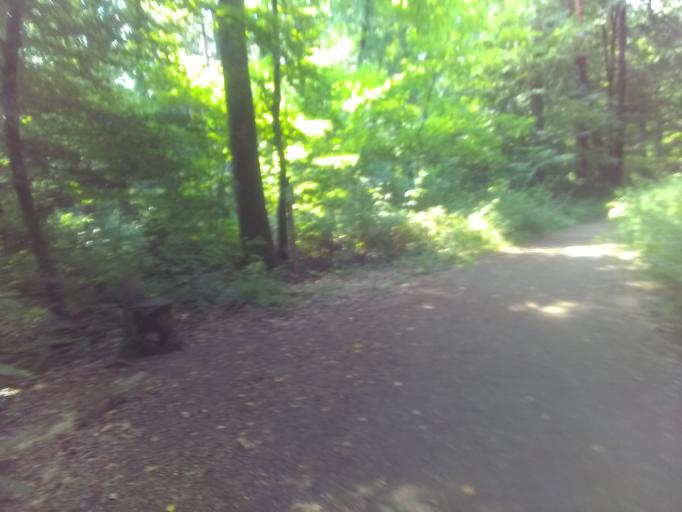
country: DE
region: Bavaria
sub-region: Upper Franconia
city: Bamberg
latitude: 49.8663
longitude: 10.8989
